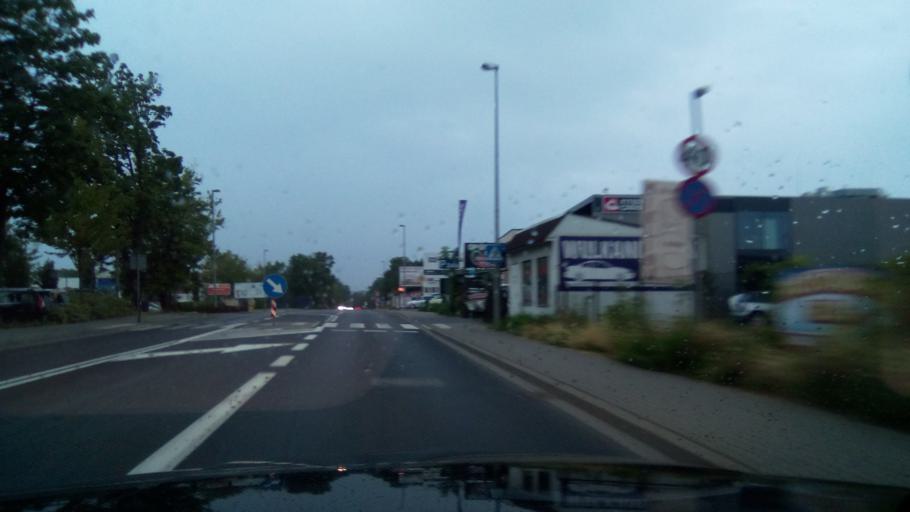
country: PL
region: Greater Poland Voivodeship
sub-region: Powiat poznanski
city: Swarzedz
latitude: 52.4186
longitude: 17.0846
